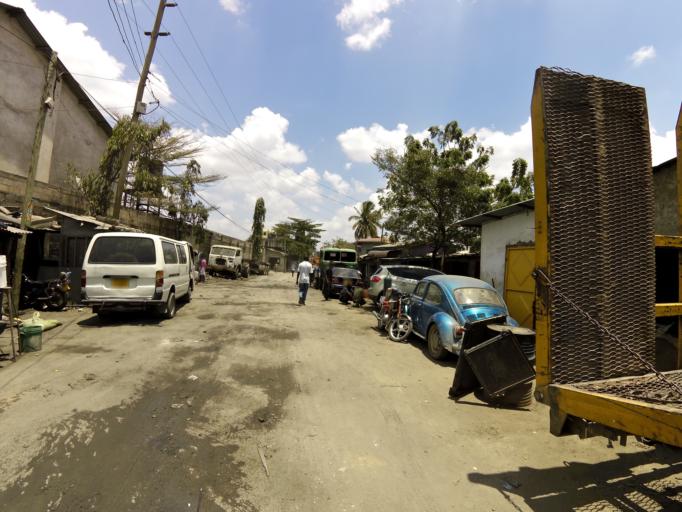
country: TZ
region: Dar es Salaam
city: Dar es Salaam
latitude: -6.8339
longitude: 39.2448
